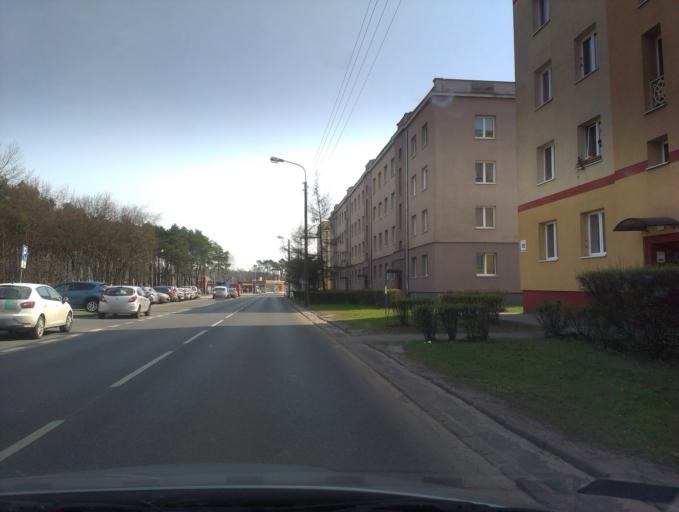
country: PL
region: Kujawsko-Pomorskie
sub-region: Bydgoszcz
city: Bydgoszcz
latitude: 53.1441
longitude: 18.0292
